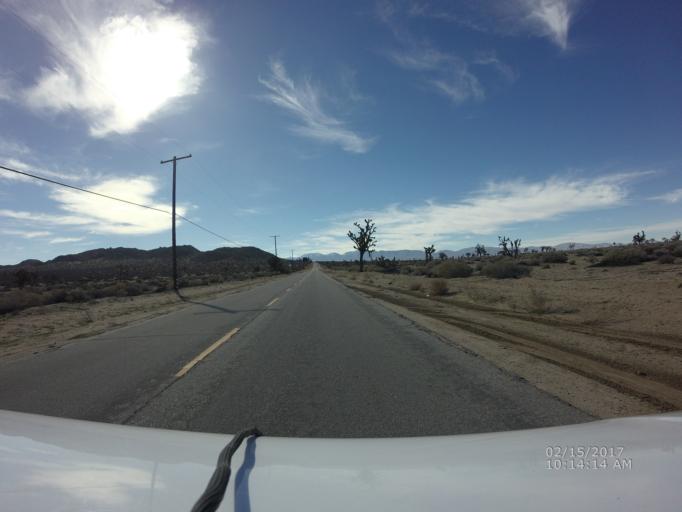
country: US
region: California
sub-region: Los Angeles County
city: Lake Los Angeles
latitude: 34.6154
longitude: -117.8716
